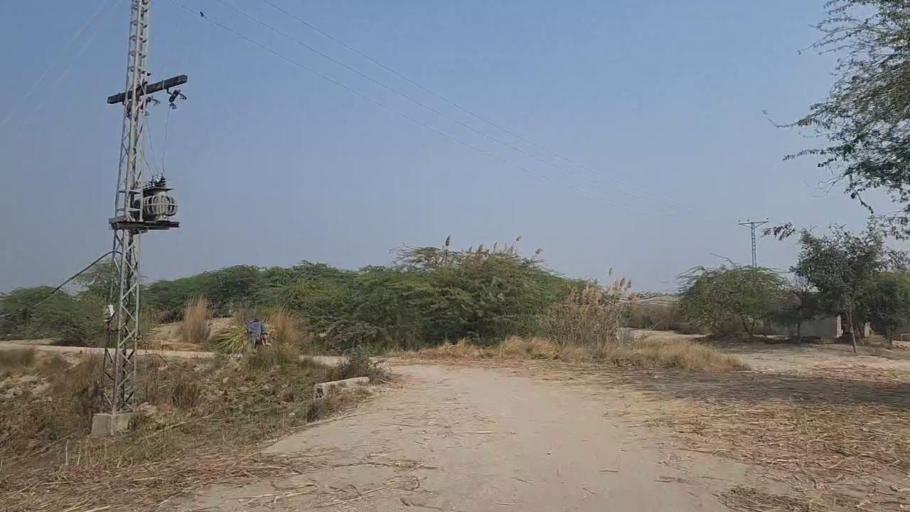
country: PK
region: Sindh
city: Daur
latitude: 26.4384
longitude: 68.4428
